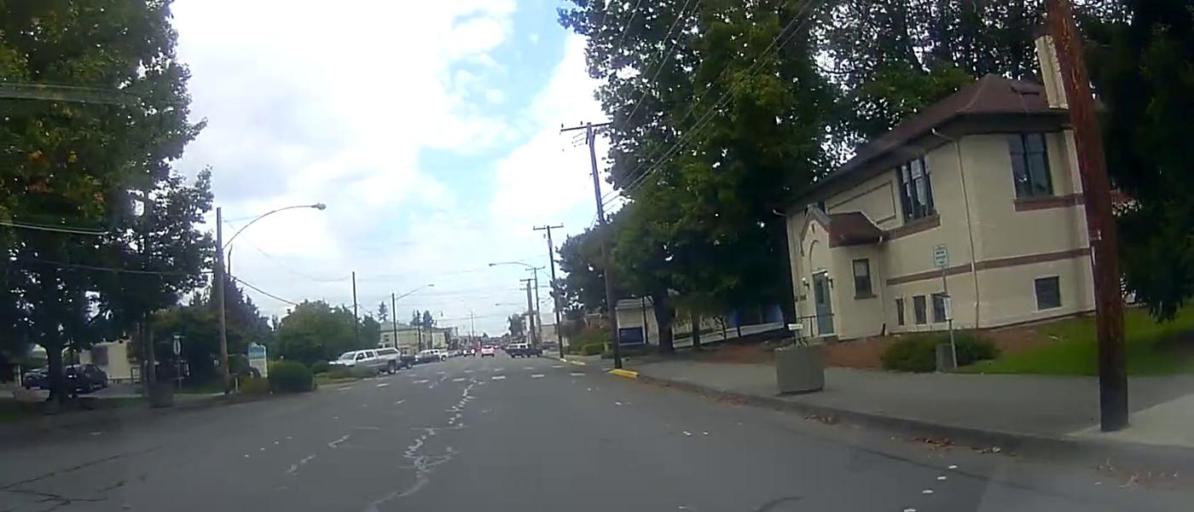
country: US
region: Washington
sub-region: Skagit County
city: Burlington
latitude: 48.4755
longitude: -122.3227
